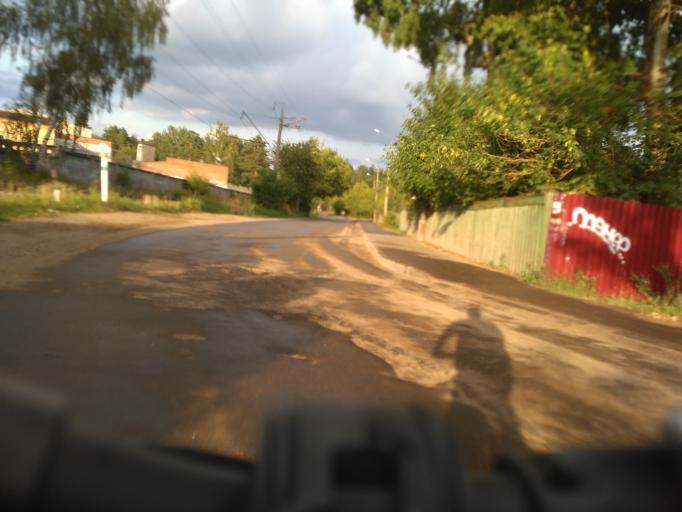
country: RU
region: Moskovskaya
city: Dubna
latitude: 56.7439
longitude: 37.1884
